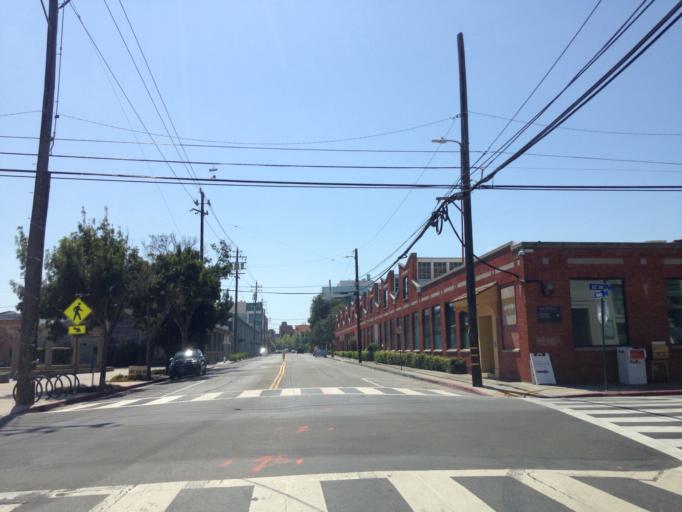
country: US
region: California
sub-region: Alameda County
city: Emeryville
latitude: 37.8432
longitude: -122.2904
